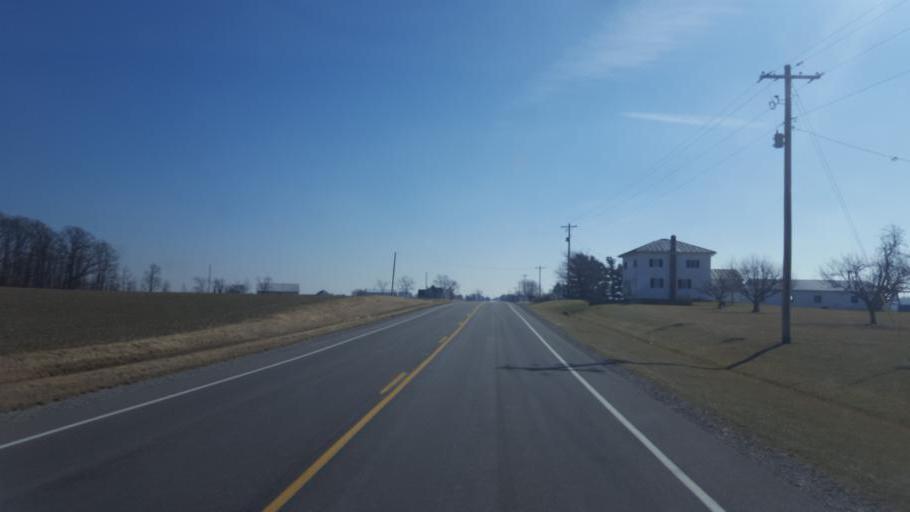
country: US
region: Ohio
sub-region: Huron County
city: Willard
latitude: 41.0489
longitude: -82.8419
